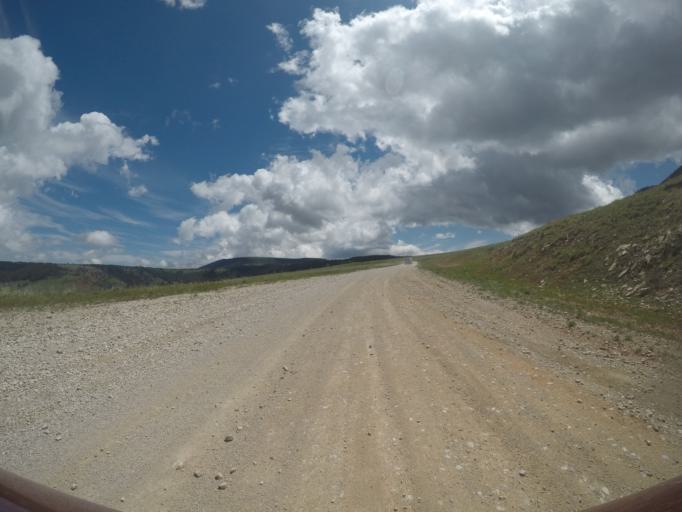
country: US
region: Wyoming
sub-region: Big Horn County
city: Lovell
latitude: 45.1894
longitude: -108.4737
